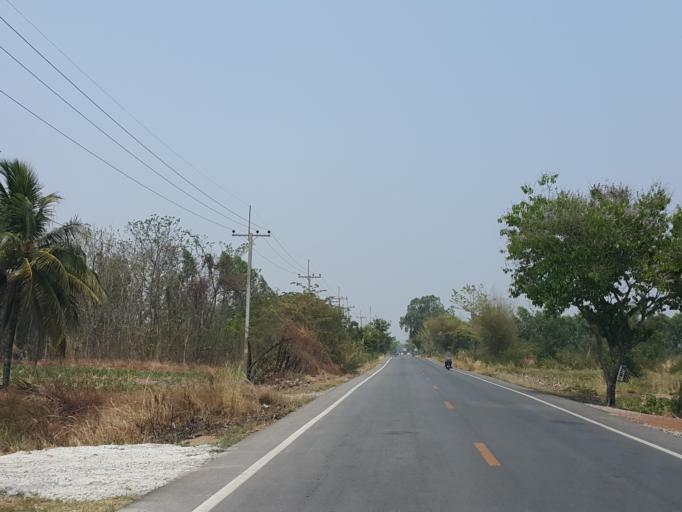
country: TH
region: Nakhon Sawan
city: Mae Wong
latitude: 15.9148
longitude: 99.4629
